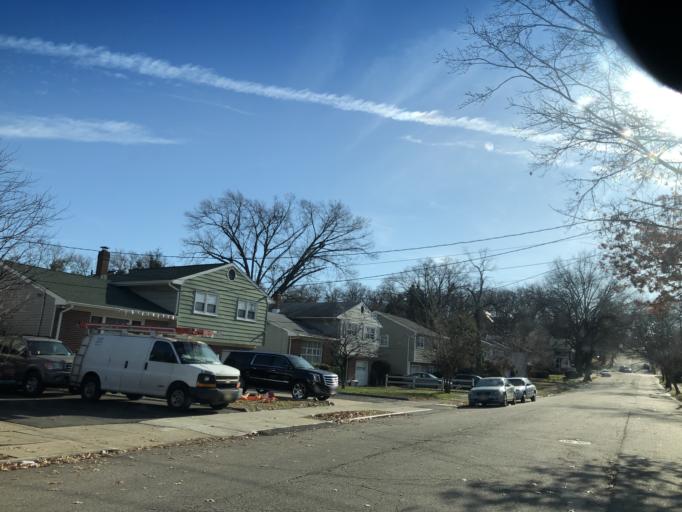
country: US
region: New Jersey
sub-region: Bergen County
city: Fair Lawn
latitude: 40.9222
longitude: -74.1373
